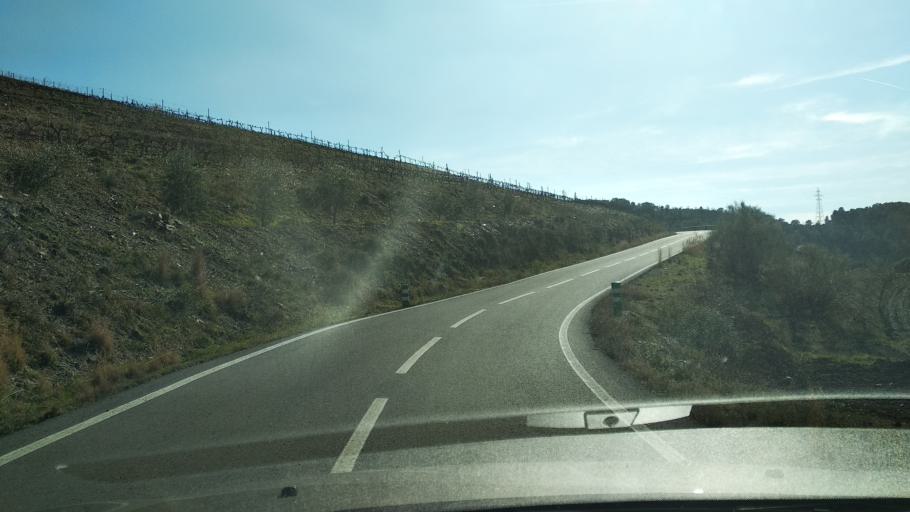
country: ES
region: Catalonia
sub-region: Provincia de Tarragona
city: el Masroig
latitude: 41.1831
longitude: 0.7465
